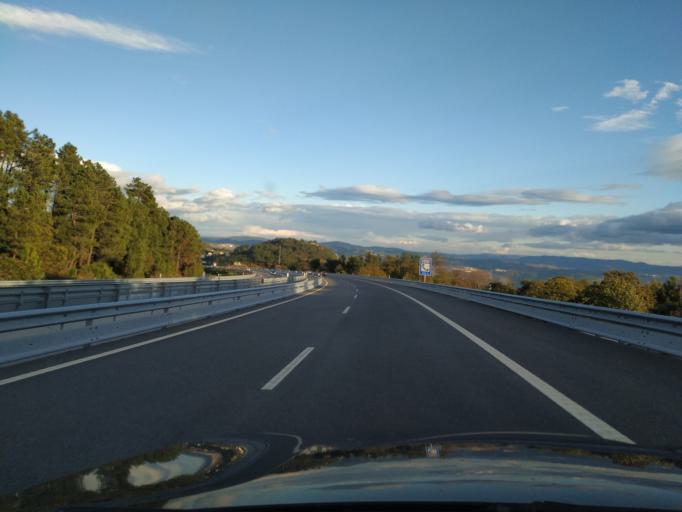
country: PT
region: Vila Real
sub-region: Santa Marta de Penaguiao
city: Santa Marta de Penaguiao
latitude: 41.2659
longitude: -7.8123
